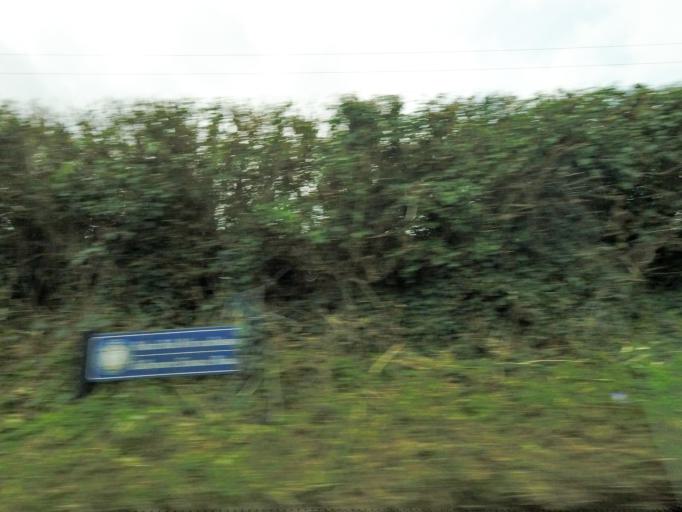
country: IE
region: Leinster
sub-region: Kildare
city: Naas
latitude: 53.1977
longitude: -6.6526
